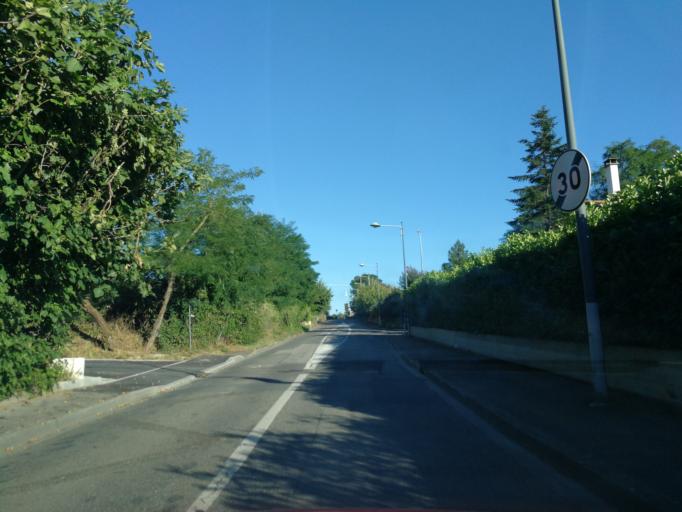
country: FR
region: Midi-Pyrenees
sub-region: Departement de la Haute-Garonne
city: Balma
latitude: 43.6203
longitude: 1.5030
